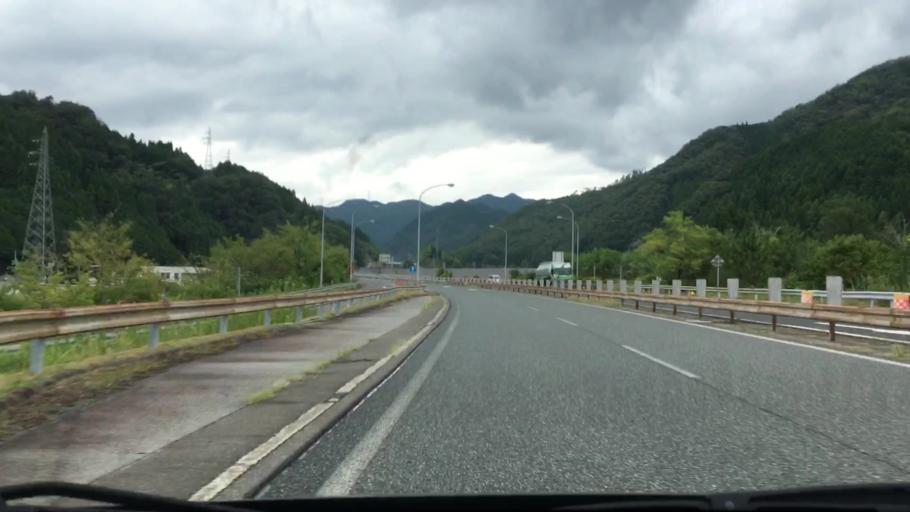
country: JP
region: Okayama
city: Niimi
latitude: 34.9983
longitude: 133.4467
